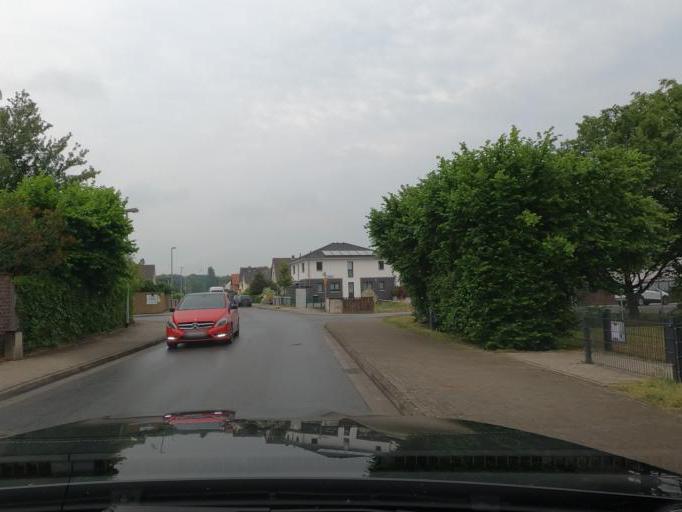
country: DE
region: Lower Saxony
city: Isernhagen Farster Bauerschaft
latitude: 52.3935
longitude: 9.8351
